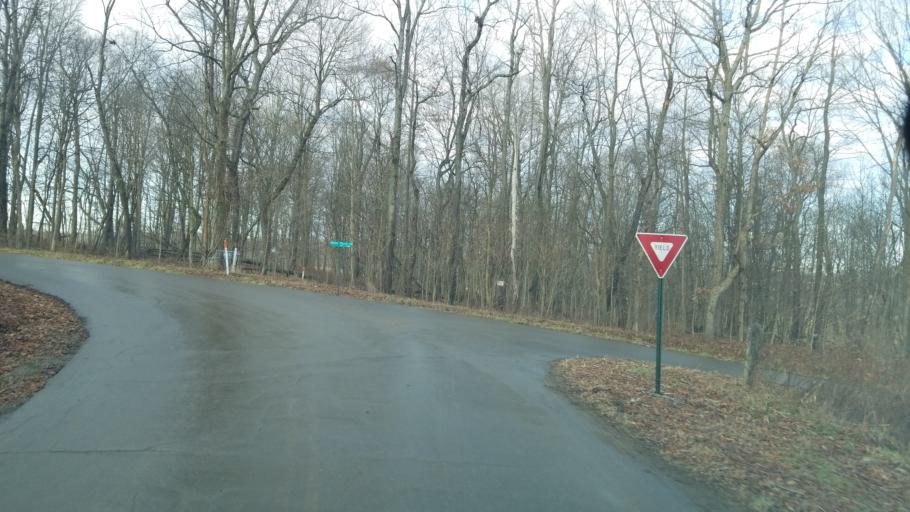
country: US
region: Ohio
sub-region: Knox County
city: Oak Hill
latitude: 40.3124
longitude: -82.2830
